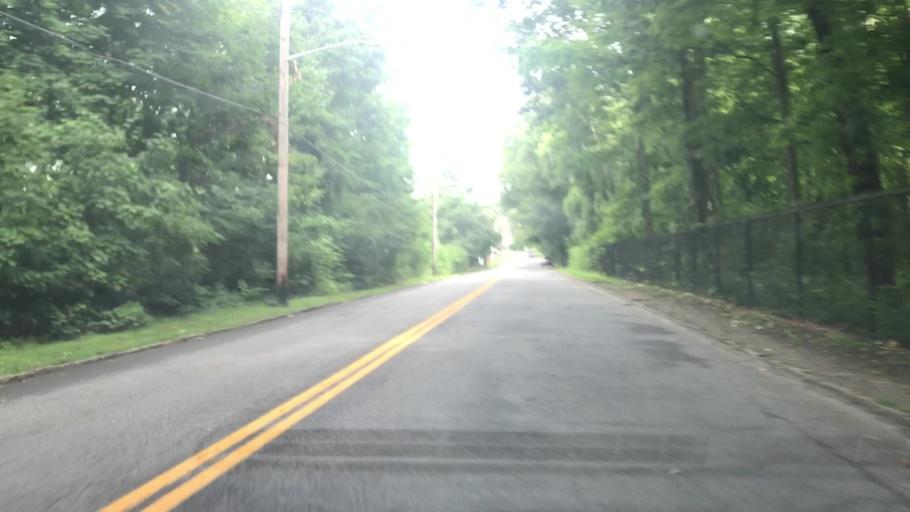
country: US
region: New York
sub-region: Westchester County
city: Tuckahoe
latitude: 40.9628
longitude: -73.8069
